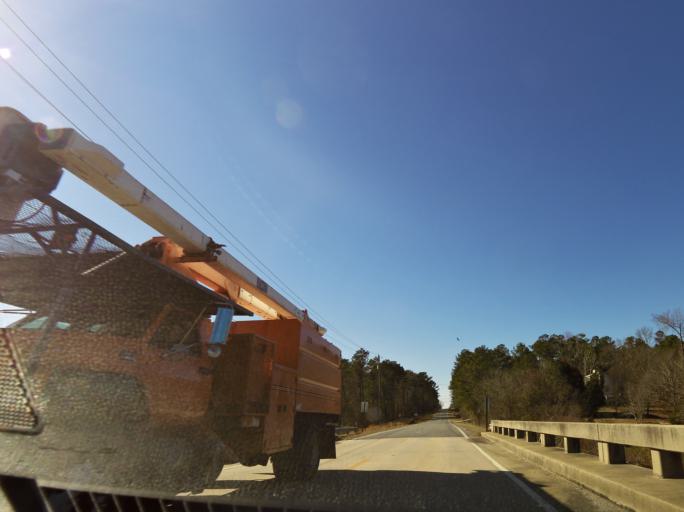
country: US
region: Georgia
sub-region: Bibb County
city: West Point
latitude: 32.8314
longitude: -83.7827
